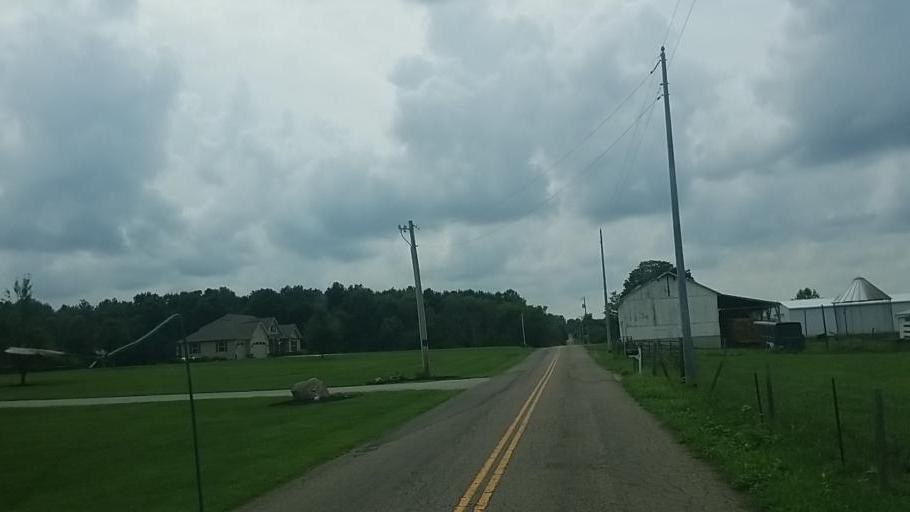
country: US
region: Ohio
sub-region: Knox County
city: Gambier
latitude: 40.3404
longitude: -82.4404
